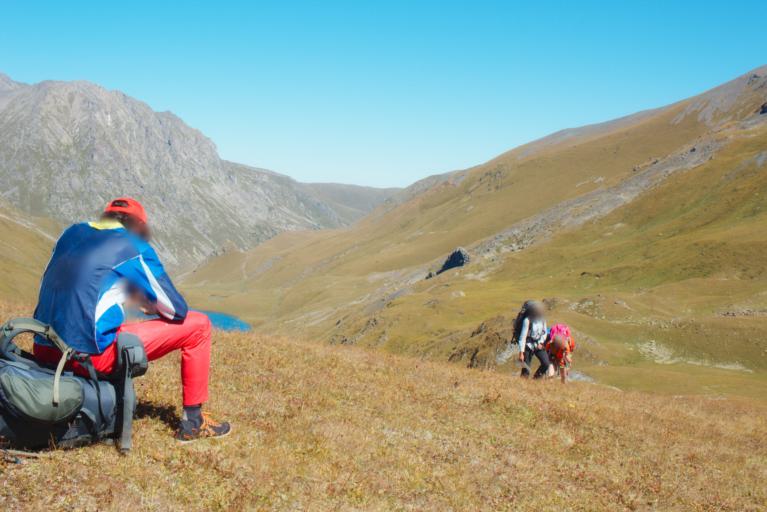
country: RU
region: Karachayevo-Cherkesiya
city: Nizhniy Arkhyz
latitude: 43.6057
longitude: 41.1567
